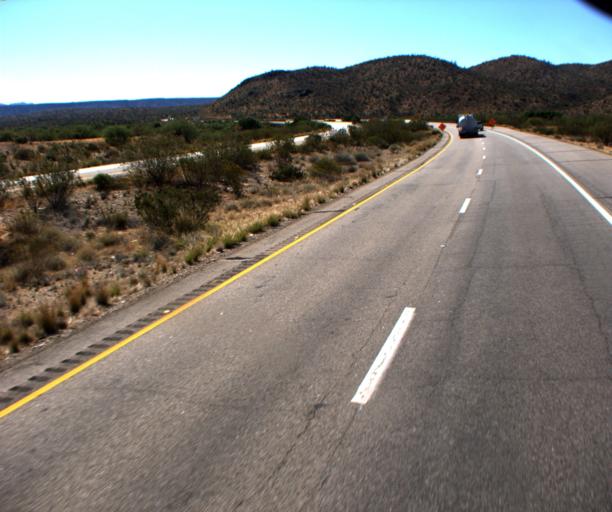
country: US
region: Arizona
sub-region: Yavapai County
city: Bagdad
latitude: 34.3719
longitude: -113.1888
